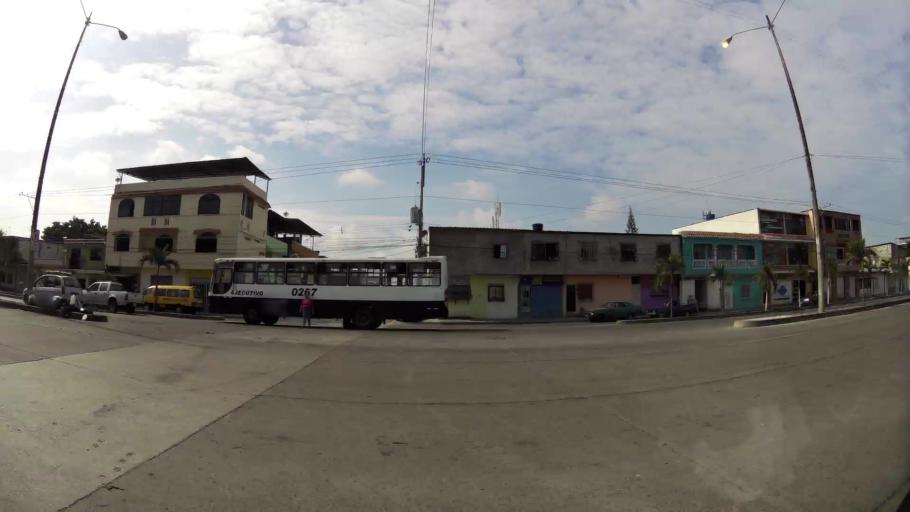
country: EC
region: Guayas
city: Guayaquil
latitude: -2.2635
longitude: -79.8932
